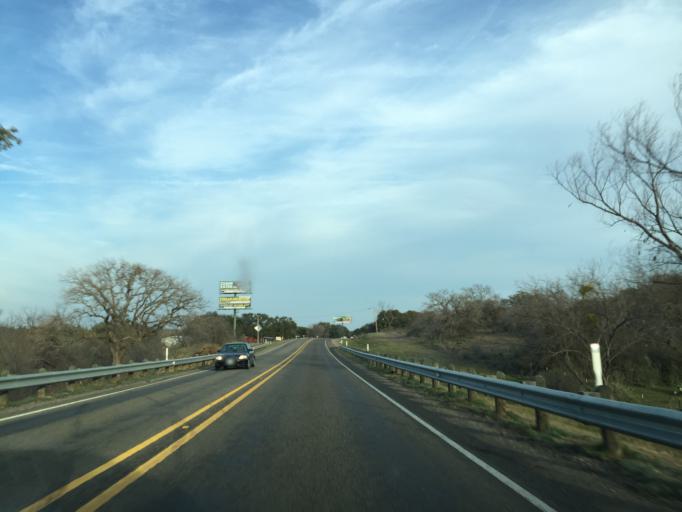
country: US
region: Texas
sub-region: Llano County
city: Llano
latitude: 30.7617
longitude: -98.6331
